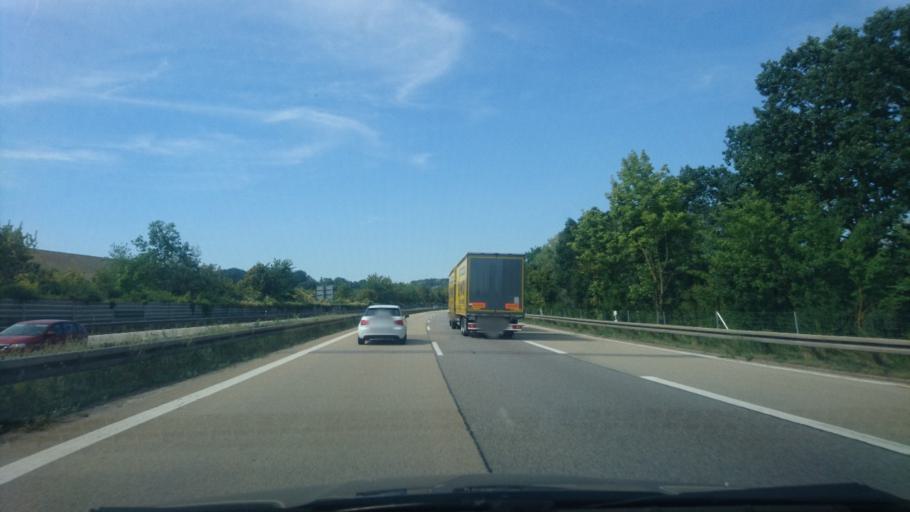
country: DE
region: Bavaria
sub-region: Upper Palatinate
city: Lappersdorf
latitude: 49.0483
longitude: 12.0933
